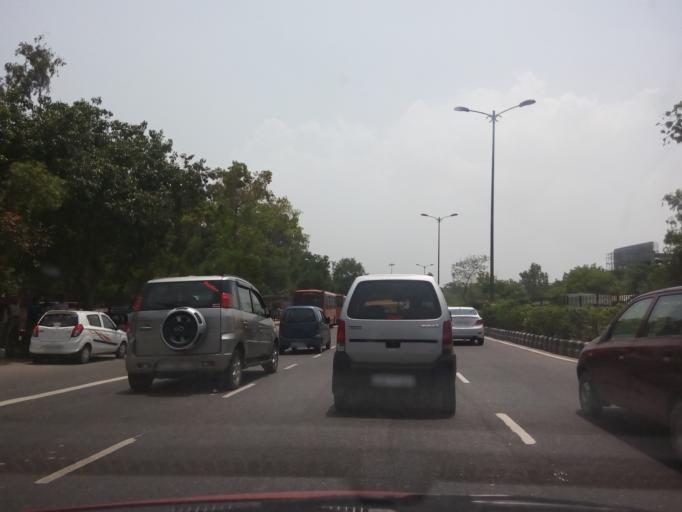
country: IN
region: NCT
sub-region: North West Delhi
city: Pitampura
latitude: 28.6589
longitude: 77.1289
